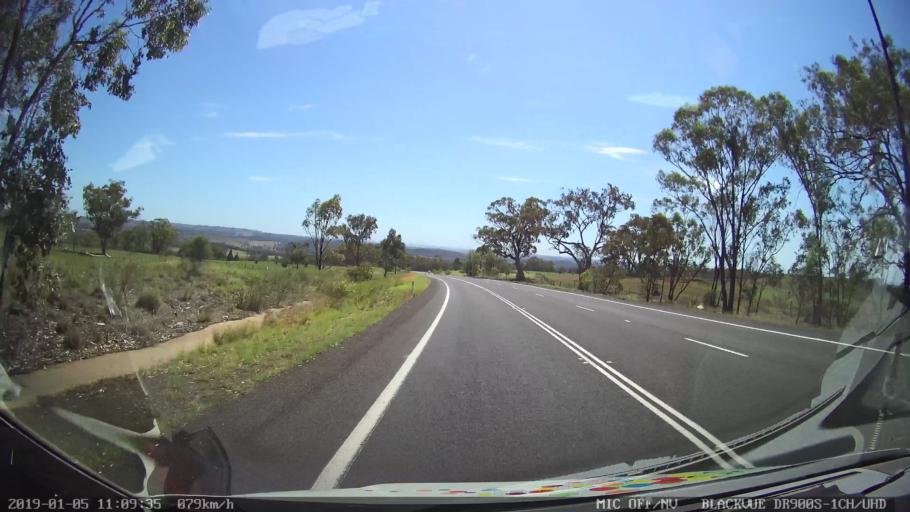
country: AU
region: New South Wales
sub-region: Warrumbungle Shire
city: Coonabarabran
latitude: -31.4127
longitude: 149.2343
